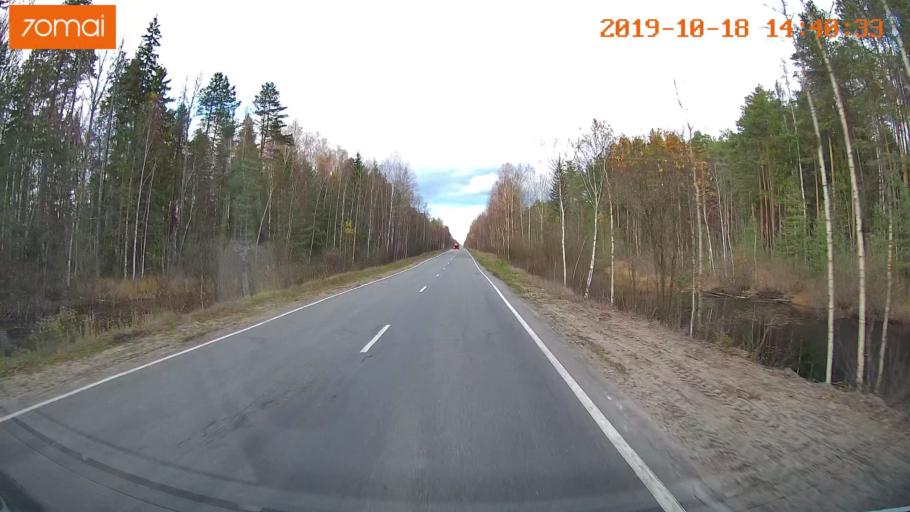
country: RU
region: Vladimir
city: Velikodvorskiy
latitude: 55.2785
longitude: 40.6692
